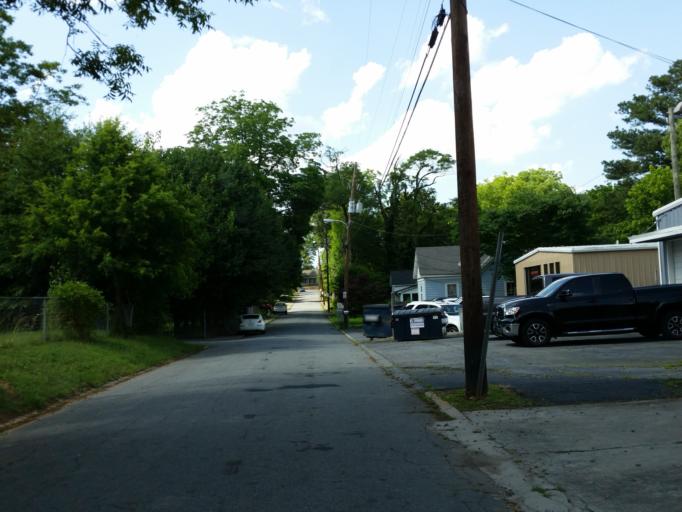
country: US
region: Georgia
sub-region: Cobb County
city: Marietta
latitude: 33.9392
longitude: -84.5412
